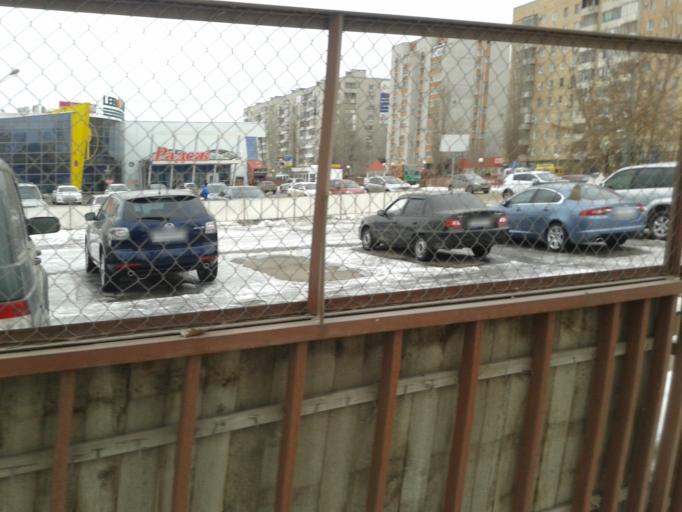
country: RU
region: Volgograd
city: Volgograd
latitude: 48.7242
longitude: 44.5153
